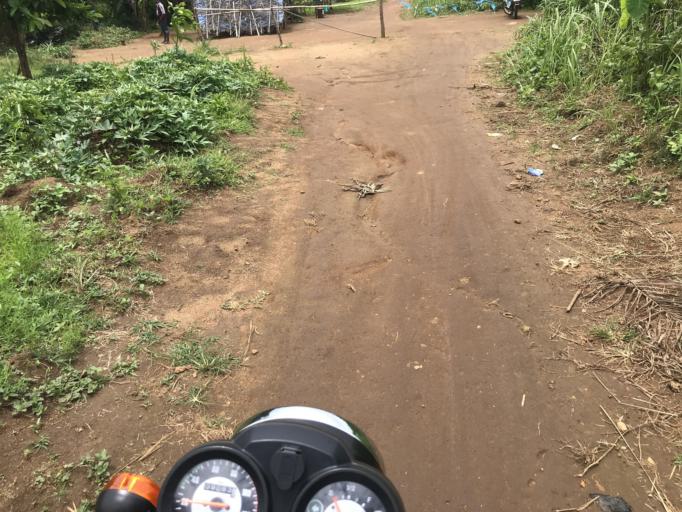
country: GN
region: Nzerekore
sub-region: Prefecture de Guekedou
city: Gueckedou
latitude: 8.4961
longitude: -10.3238
